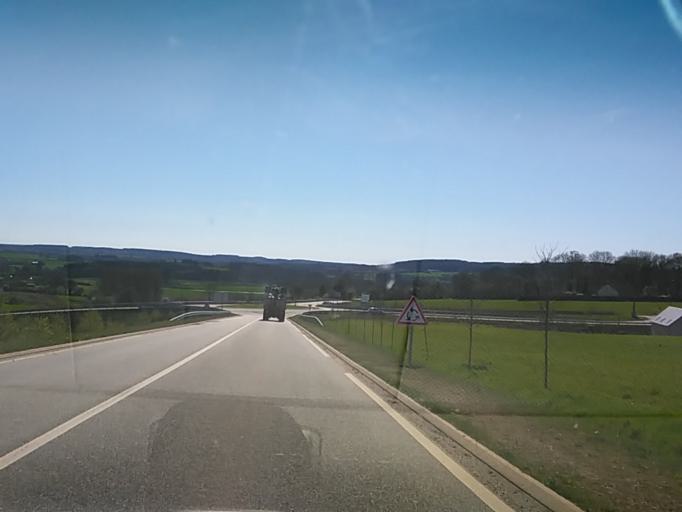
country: FR
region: Pays de la Loire
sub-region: Departement de la Mayenne
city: Pre-en-Pail
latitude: 48.5659
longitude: -0.1362
